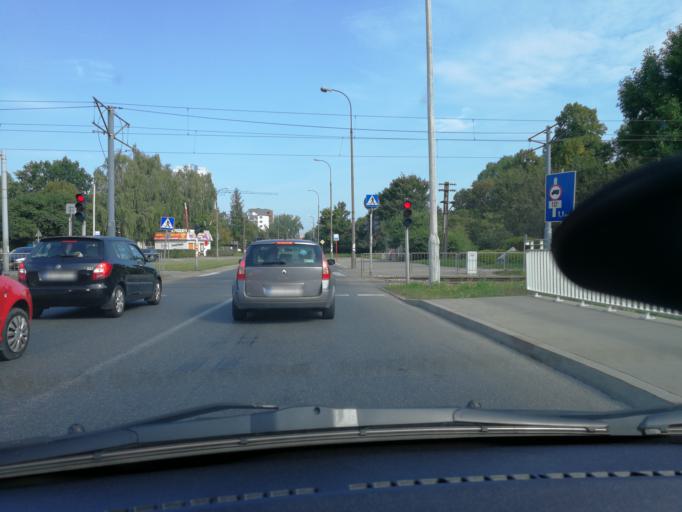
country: PL
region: Masovian Voivodeship
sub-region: Warszawa
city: Ochota
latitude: 52.2265
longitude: 20.9428
